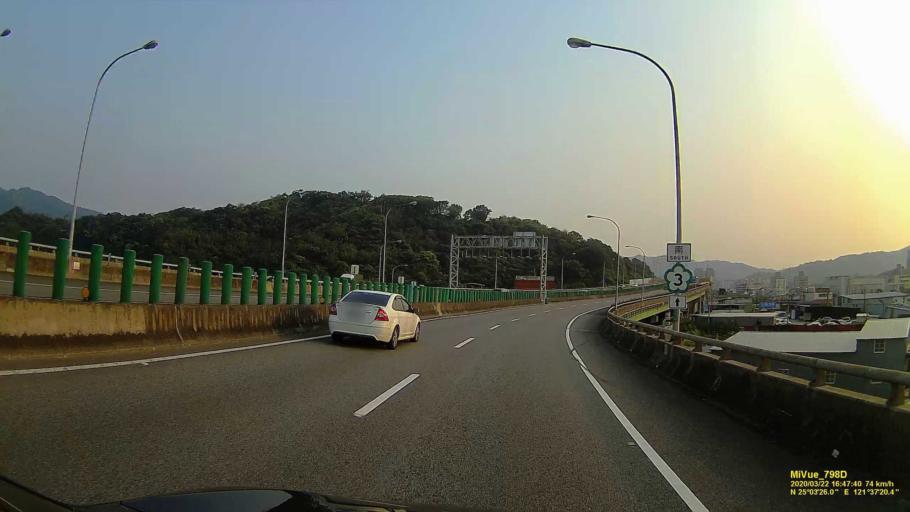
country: TW
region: Taipei
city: Taipei
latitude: 25.0568
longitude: 121.6224
